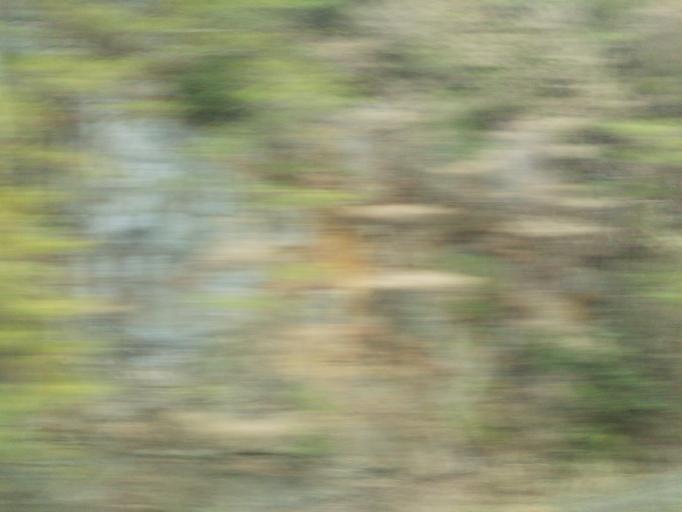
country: JP
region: Kochi
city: Nakamura
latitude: 32.9893
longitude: 132.9629
